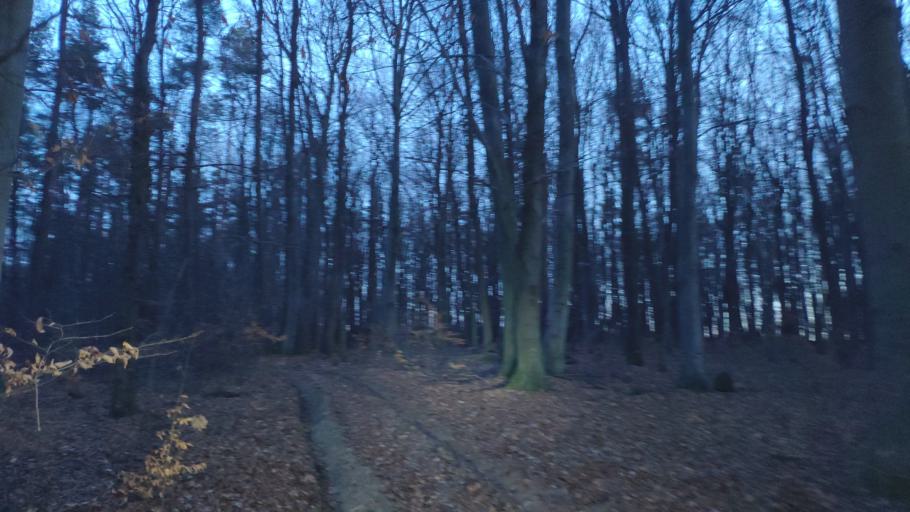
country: SK
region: Kosicky
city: Kosice
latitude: 48.8340
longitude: 21.2490
